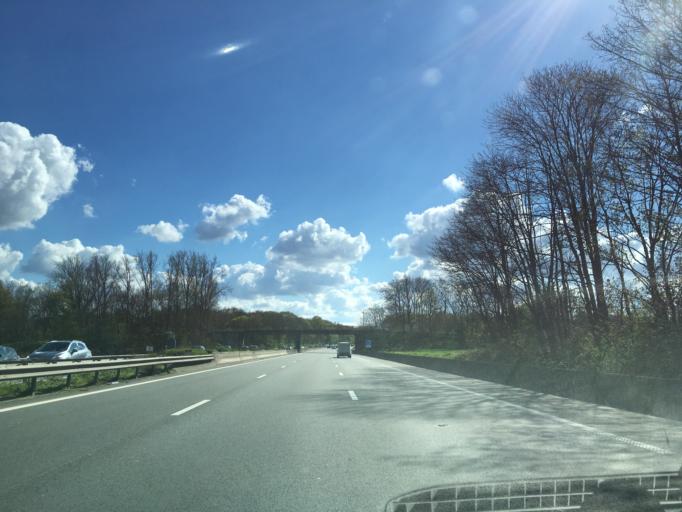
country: FR
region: Nord-Pas-de-Calais
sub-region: Departement du Nord
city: Phalempin
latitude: 50.5195
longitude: 3.0382
